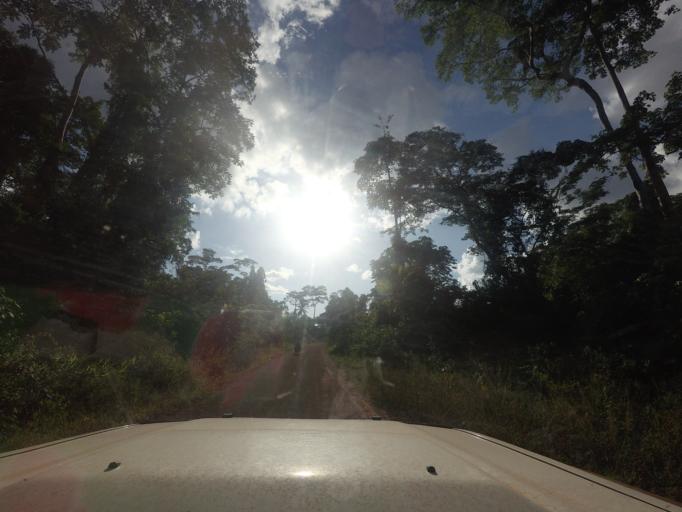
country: LR
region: Grand Gedeh
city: Zwedru
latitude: 6.0204
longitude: -8.0724
